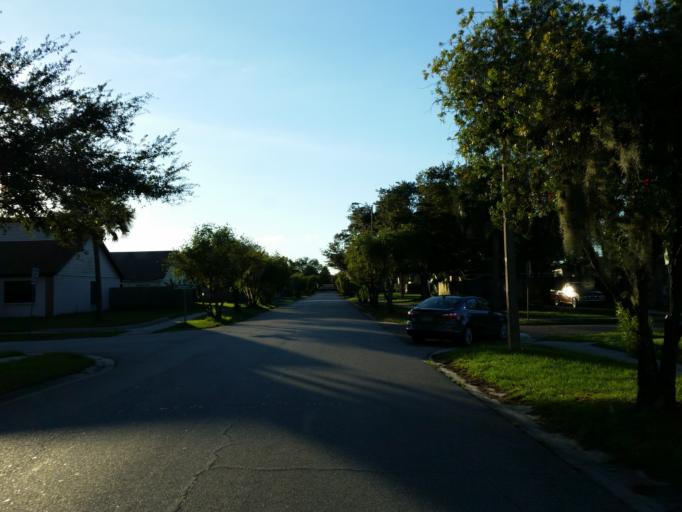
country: US
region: Florida
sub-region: Hillsborough County
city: Brandon
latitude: 27.9166
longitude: -82.3154
